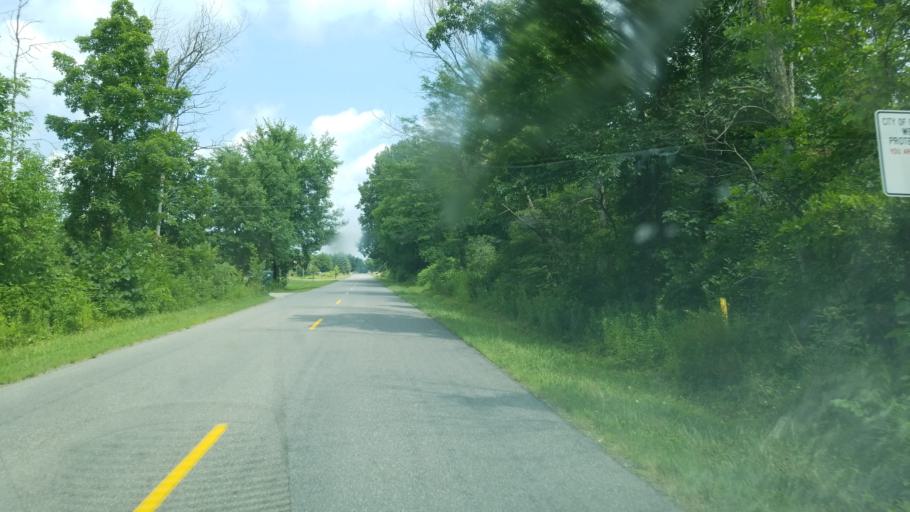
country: US
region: Michigan
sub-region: Kent County
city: Cedar Springs
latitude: 43.2281
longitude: -85.5109
